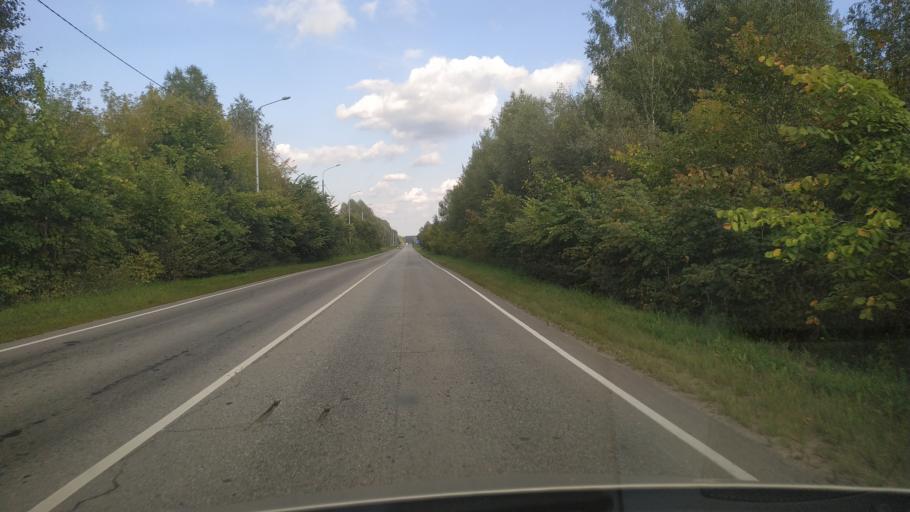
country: RU
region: Moskovskaya
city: Vereya
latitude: 55.7081
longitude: 39.1143
